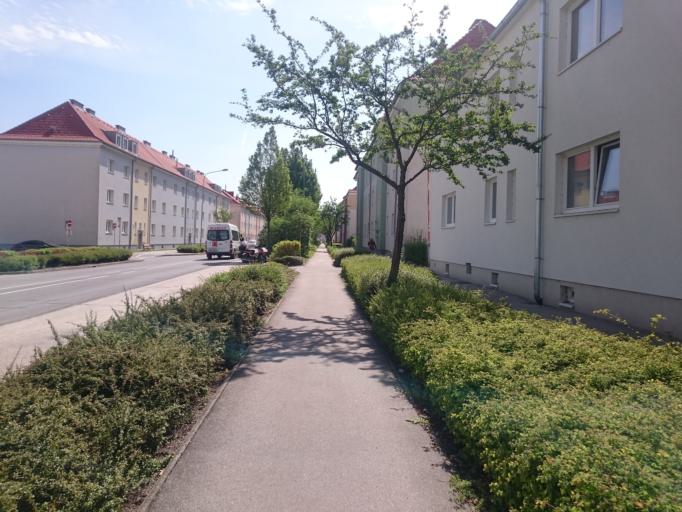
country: AT
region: Lower Austria
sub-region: Politischer Bezirk Korneuburg
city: Korneuburg
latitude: 48.3495
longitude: 16.3261
